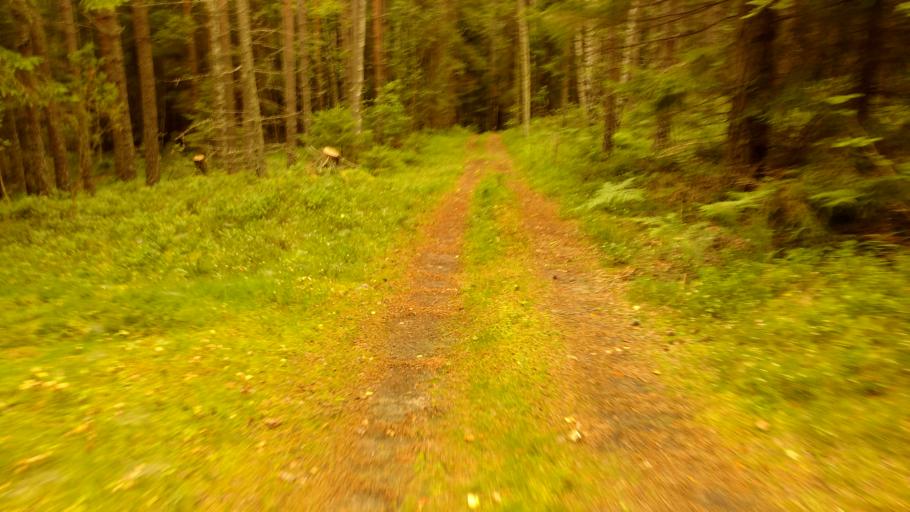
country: FI
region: Varsinais-Suomi
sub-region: Salo
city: Pertteli
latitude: 60.4015
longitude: 23.2206
